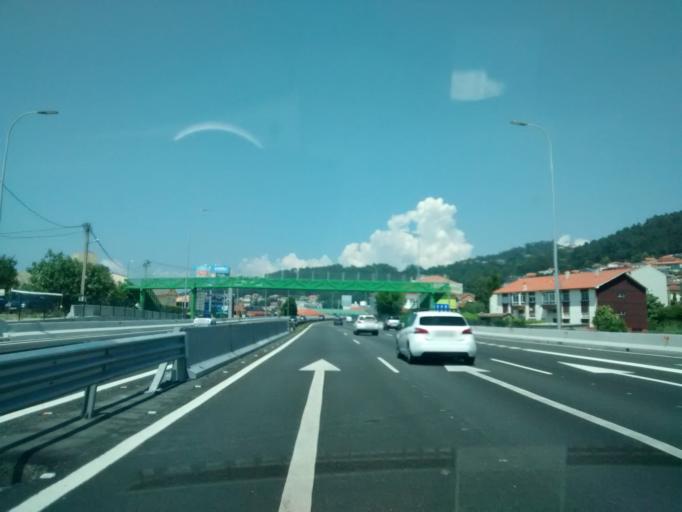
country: ES
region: Galicia
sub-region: Provincia de Pontevedra
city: Vigo
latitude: 42.2632
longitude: -8.6702
